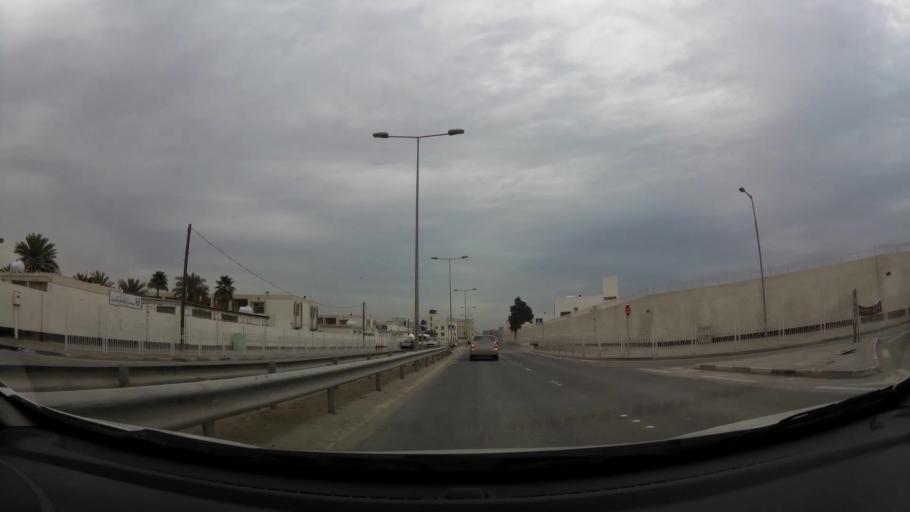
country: BH
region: Northern
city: Sitrah
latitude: 26.1547
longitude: 50.6201
